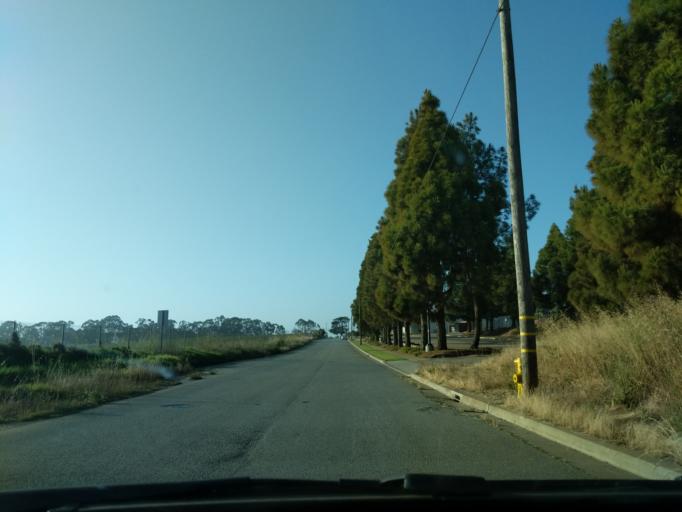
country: US
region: California
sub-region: Monterey County
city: Las Lomas
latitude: 36.8685
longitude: -121.7624
